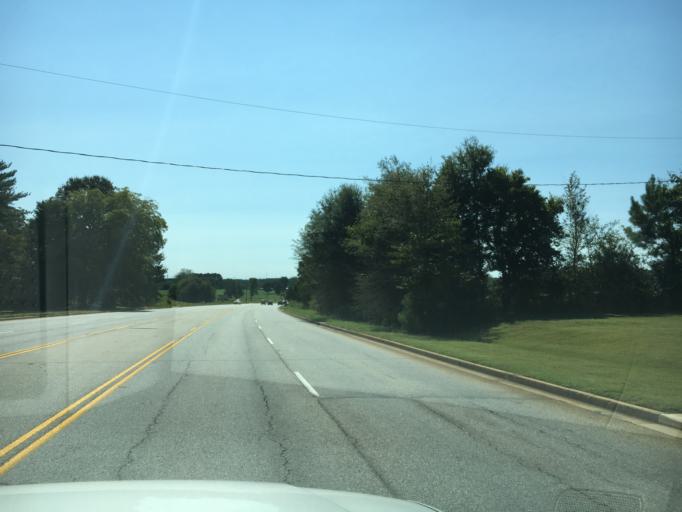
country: US
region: South Carolina
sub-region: Spartanburg County
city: Roebuck
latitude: 34.8739
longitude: -82.0378
